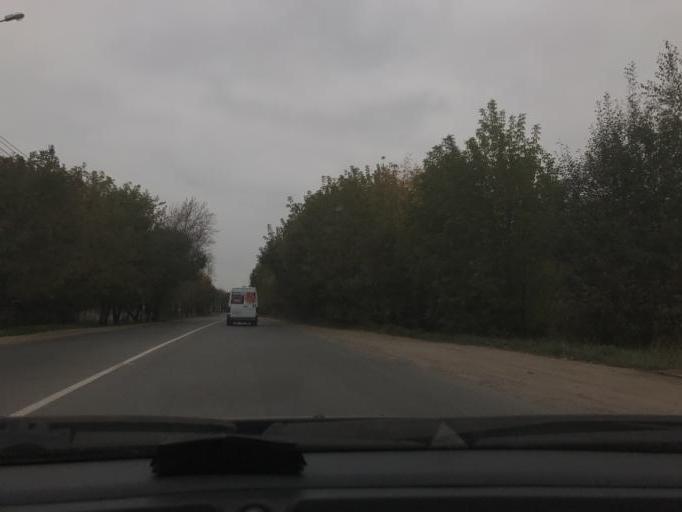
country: RU
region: Kaluga
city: Kaluga
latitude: 54.5155
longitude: 36.3216
